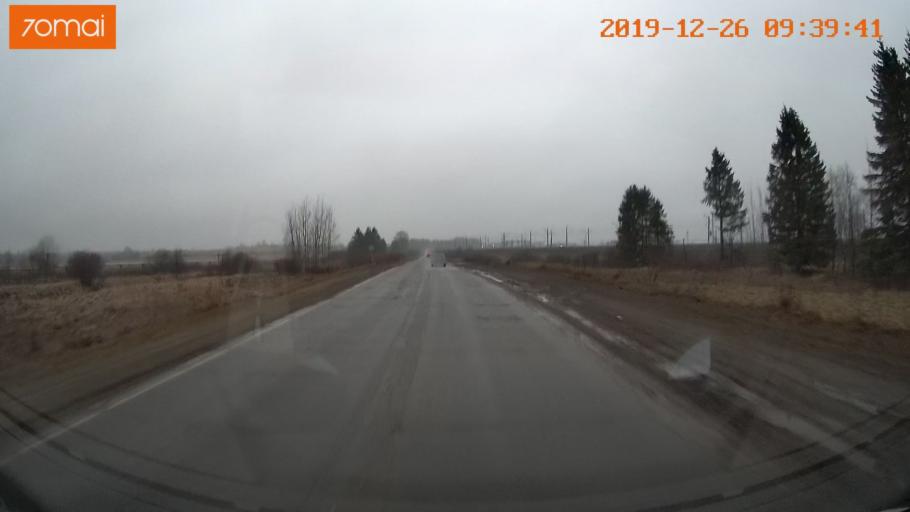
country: RU
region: Vologda
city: Vologda
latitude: 59.1566
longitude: 40.0209
